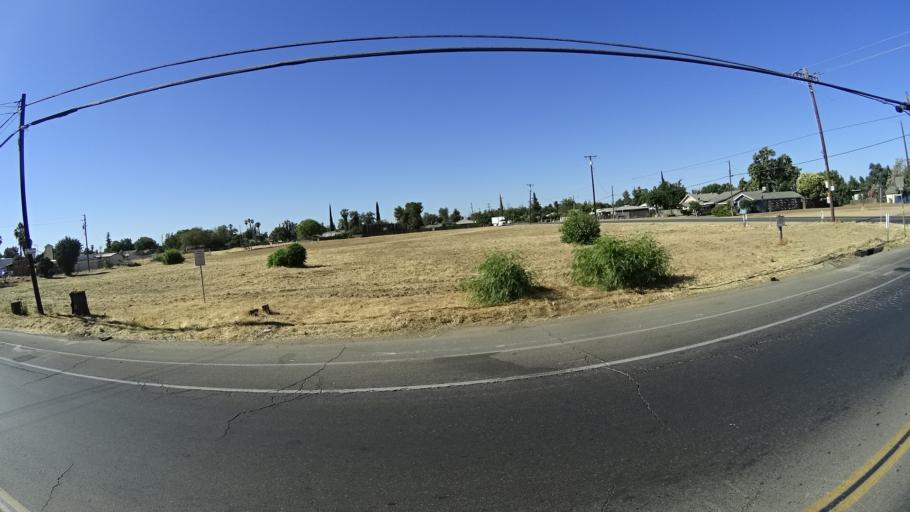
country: US
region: California
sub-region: Fresno County
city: West Park
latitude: 36.7575
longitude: -119.8351
